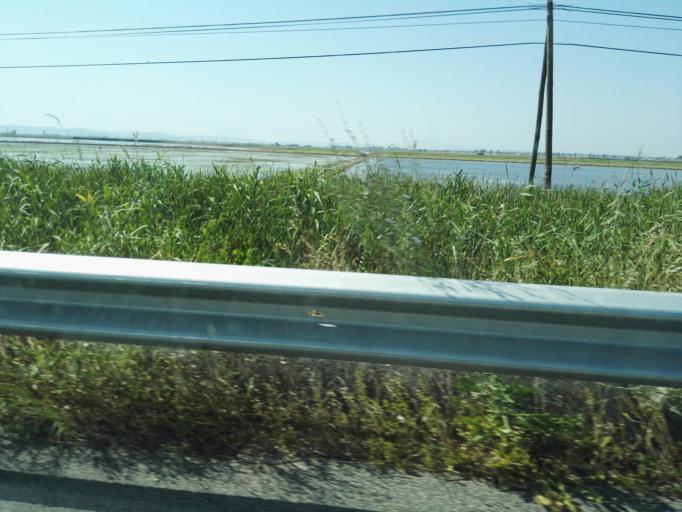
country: PT
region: Santarem
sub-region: Benavente
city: Samora Correia
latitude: 38.9419
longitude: -8.8385
